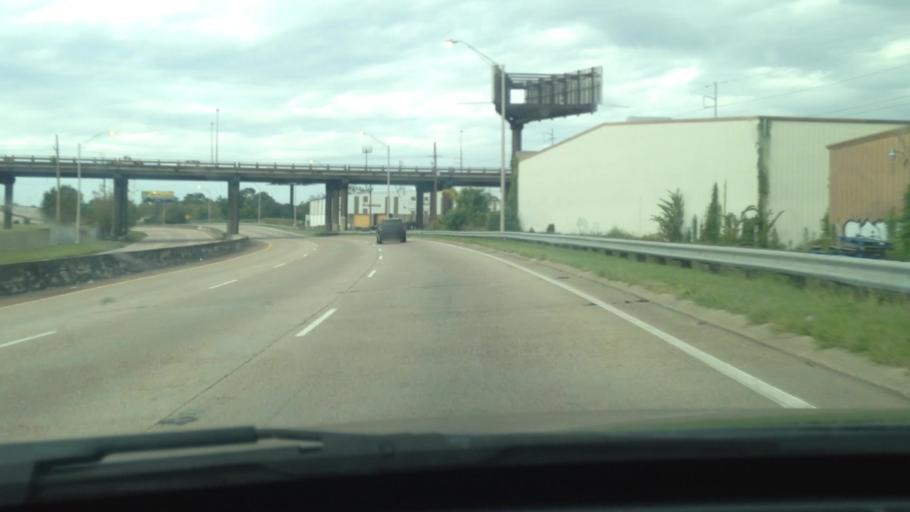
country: US
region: Louisiana
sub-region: Jefferson Parish
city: Jefferson
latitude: 29.9717
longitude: -90.1550
